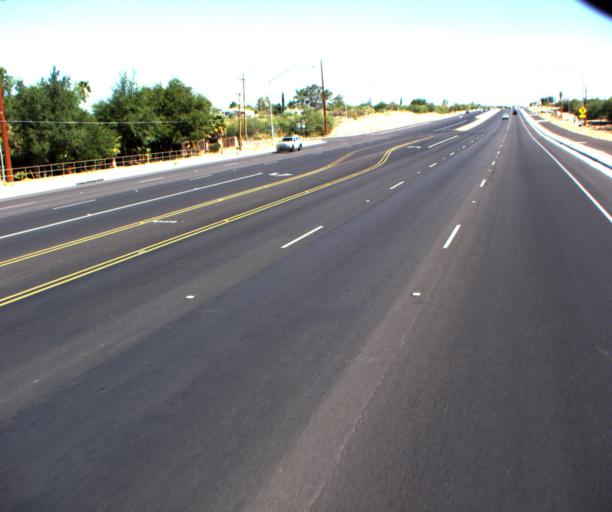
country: US
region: Arizona
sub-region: Pima County
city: Catalina
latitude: 32.4847
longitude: -110.9224
